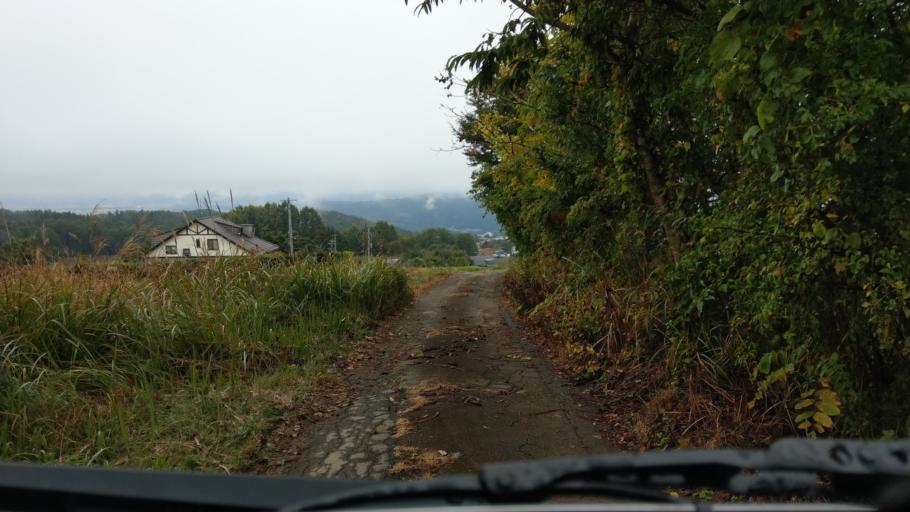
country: JP
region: Nagano
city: Komoro
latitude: 36.3584
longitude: 138.4450
